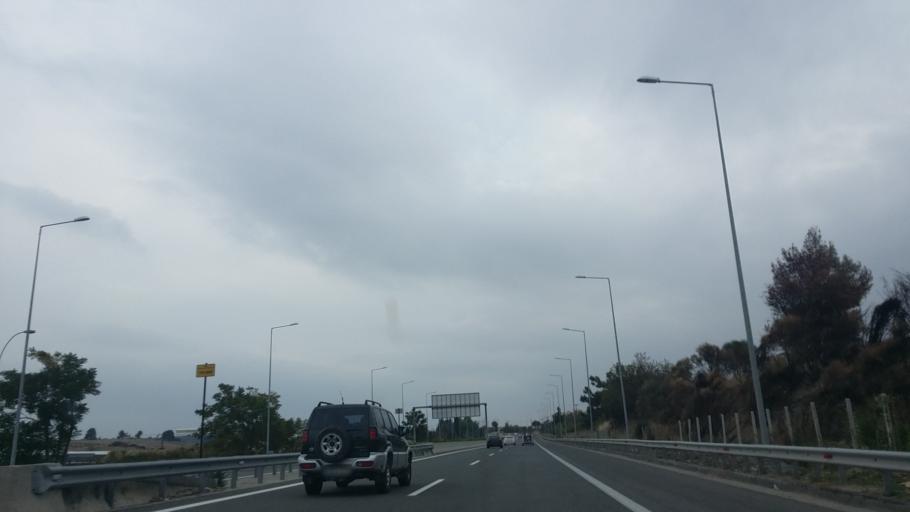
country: GR
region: Central Greece
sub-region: Nomos Voiotias
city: Arma
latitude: 38.3787
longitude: 23.5019
